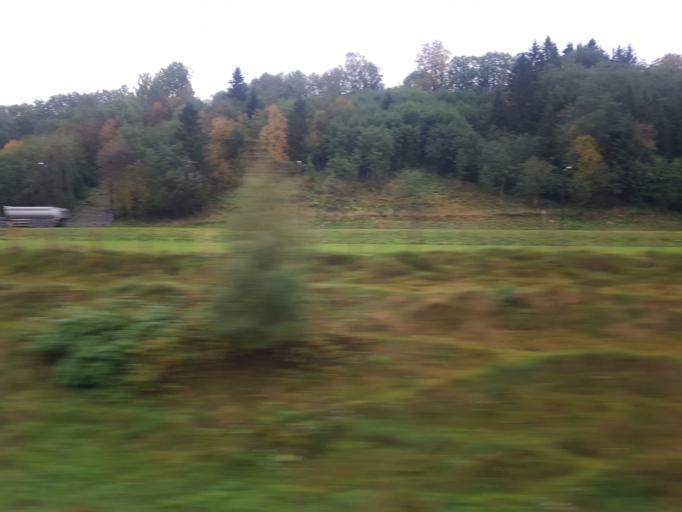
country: NO
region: Sor-Trondelag
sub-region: Melhus
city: Lundamo
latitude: 63.1387
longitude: 10.2611
